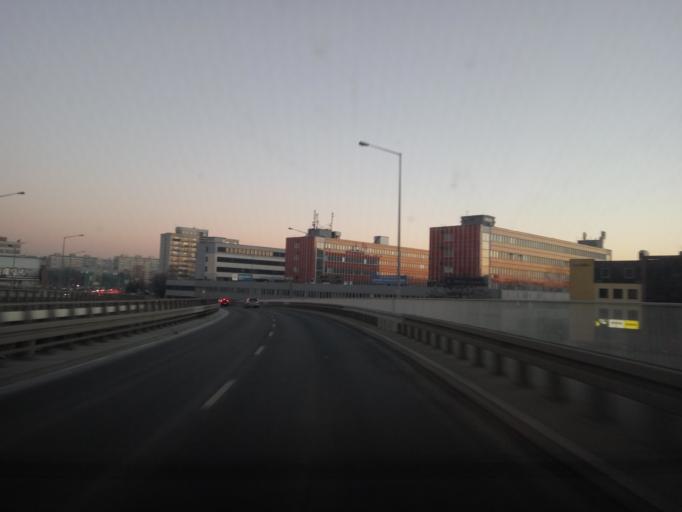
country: PL
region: Lower Silesian Voivodeship
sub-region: Powiat wroclawski
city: Wroclaw
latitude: 51.0969
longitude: 16.9748
